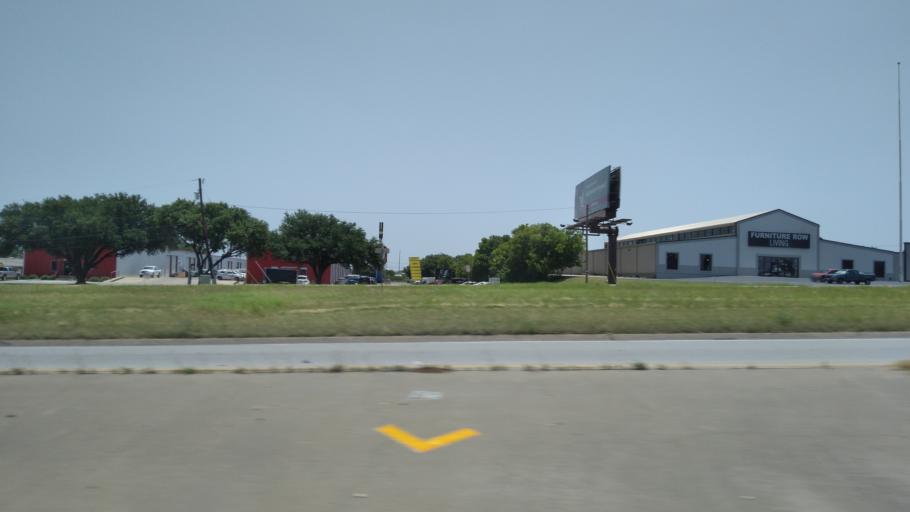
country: US
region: Texas
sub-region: McLennan County
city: Woodway
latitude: 31.5136
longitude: -97.1864
